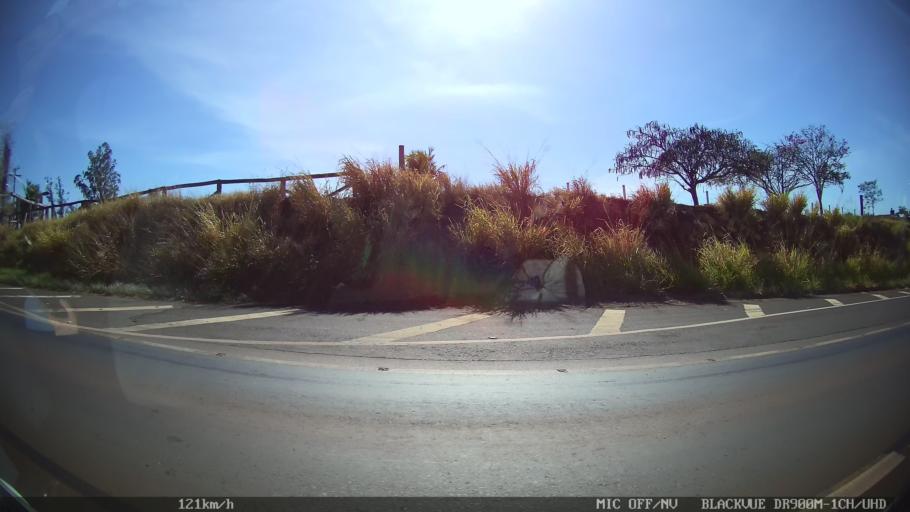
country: BR
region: Sao Paulo
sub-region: Barretos
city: Barretos
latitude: -20.5411
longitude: -48.6161
